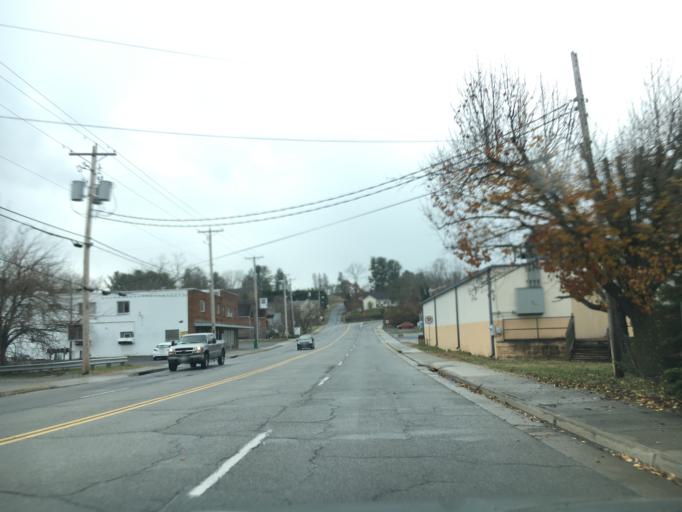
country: US
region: Virginia
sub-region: Montgomery County
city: Christiansburg
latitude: 37.1276
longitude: -80.4095
